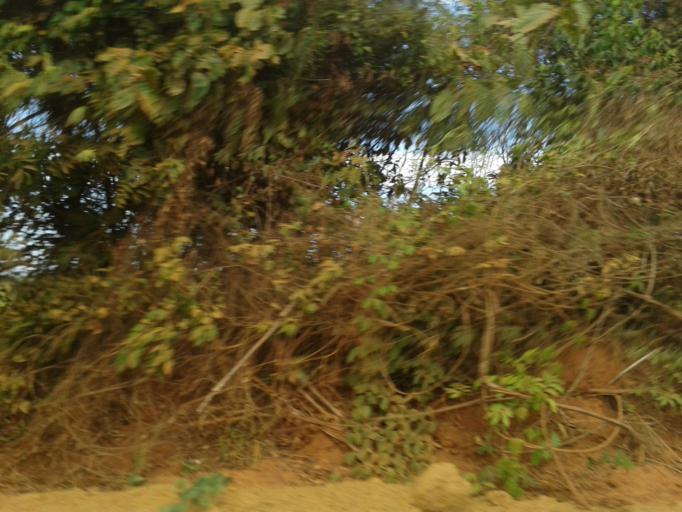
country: BR
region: Minas Gerais
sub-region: Ituiutaba
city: Ituiutaba
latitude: -19.0457
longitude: -49.3707
